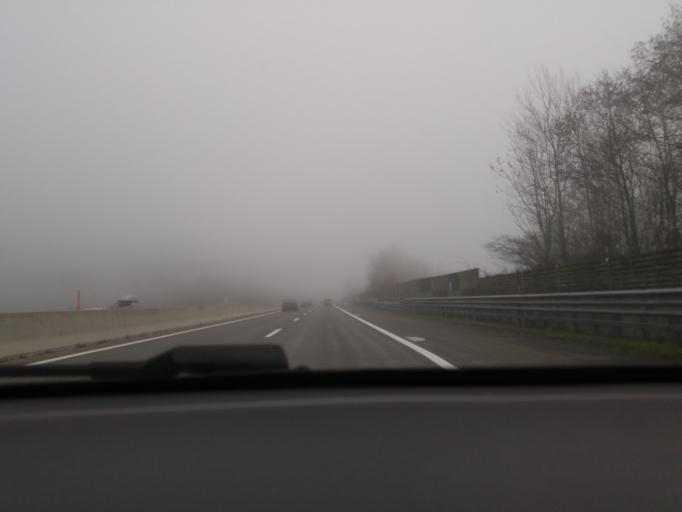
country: AT
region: Upper Austria
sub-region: Politischer Bezirk Vocklabruck
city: Seewalchen
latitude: 47.9570
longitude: 13.5568
